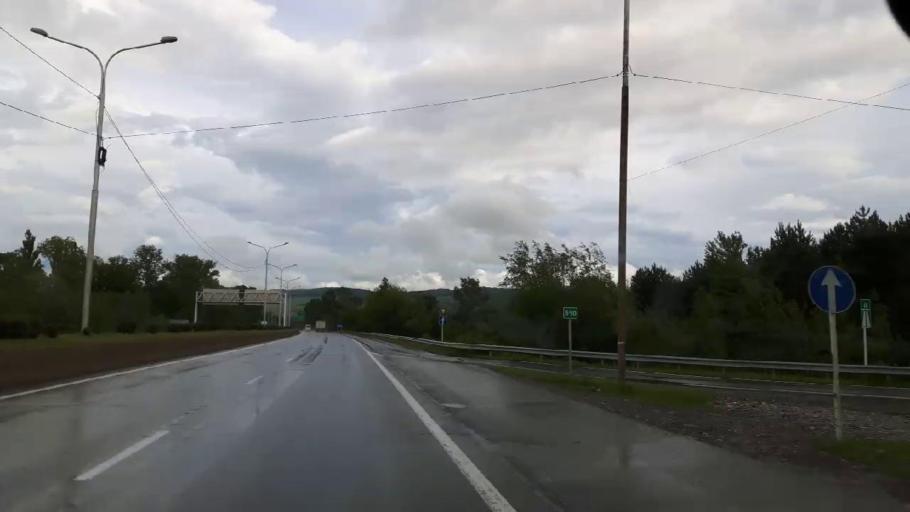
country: GE
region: Shida Kartli
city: Kaspi
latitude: 41.9132
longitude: 44.5608
